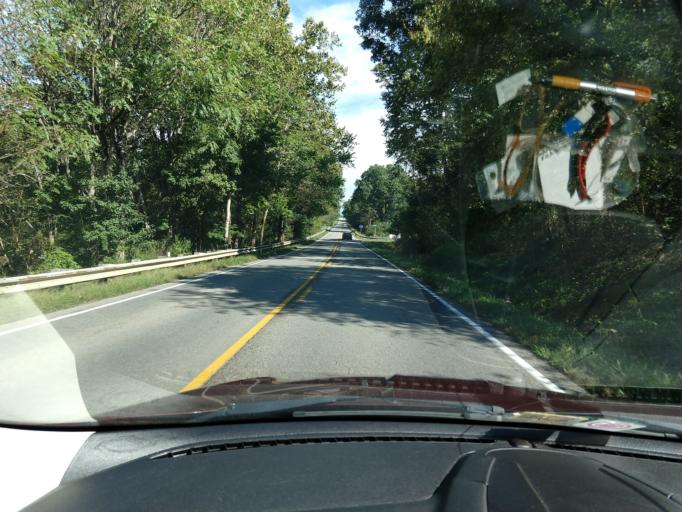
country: US
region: Virginia
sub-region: Augusta County
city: Crimora
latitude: 38.1836
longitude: -78.8424
